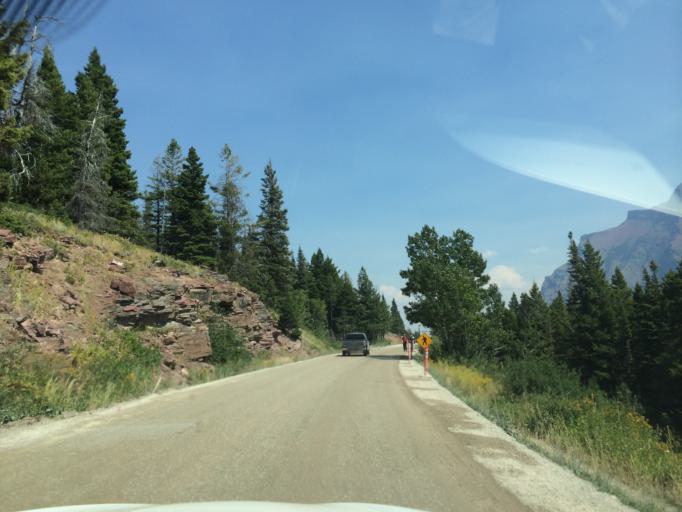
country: US
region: Montana
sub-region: Glacier County
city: Browning
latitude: 48.6749
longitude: -113.6073
